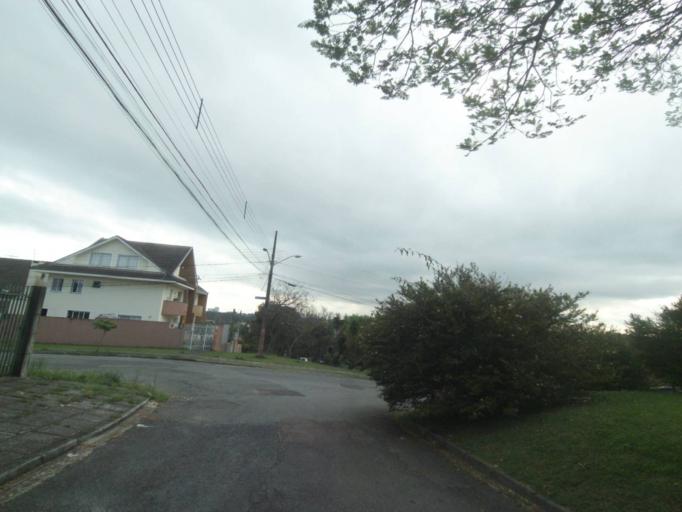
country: BR
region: Parana
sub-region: Pinhais
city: Pinhais
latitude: -25.4173
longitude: -49.2102
